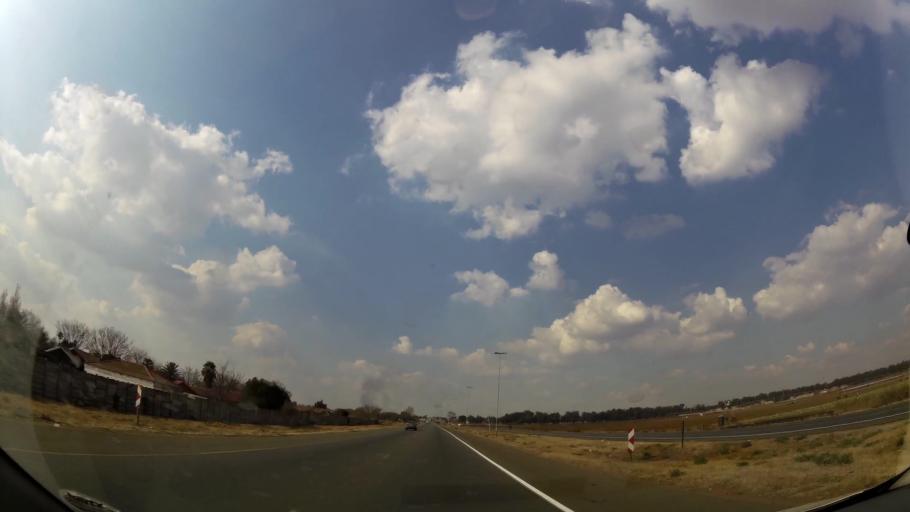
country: ZA
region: Gauteng
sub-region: Ekurhuleni Metropolitan Municipality
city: Germiston
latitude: -26.2938
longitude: 28.2148
